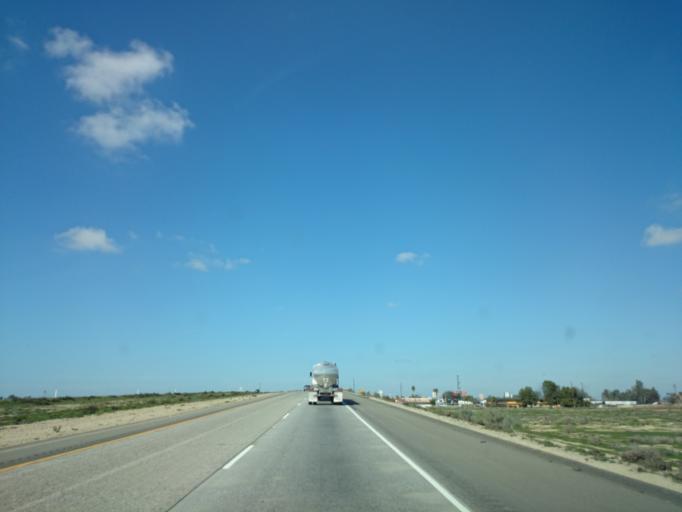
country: US
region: California
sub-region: Kern County
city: Buttonwillow
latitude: 35.3958
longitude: -119.3928
